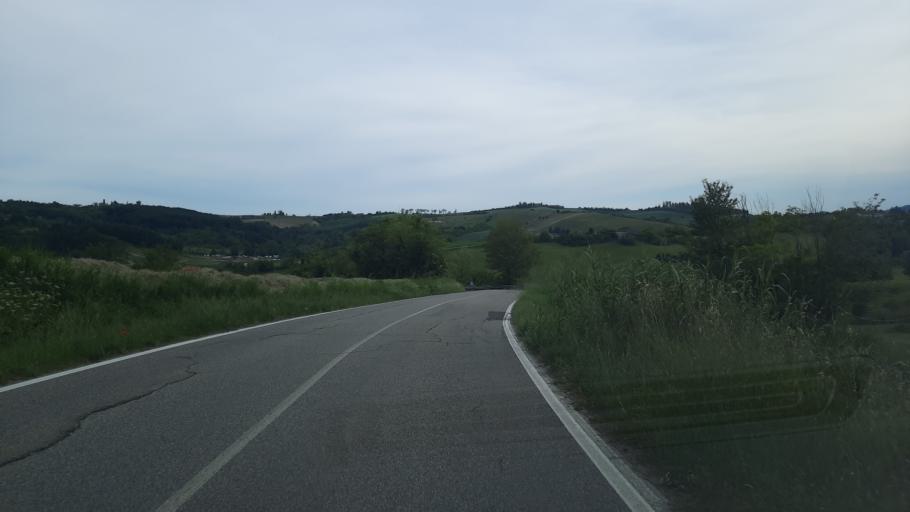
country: IT
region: Piedmont
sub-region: Provincia di Alessandria
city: Coniolo Bricco
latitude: 45.1451
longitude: 8.3802
